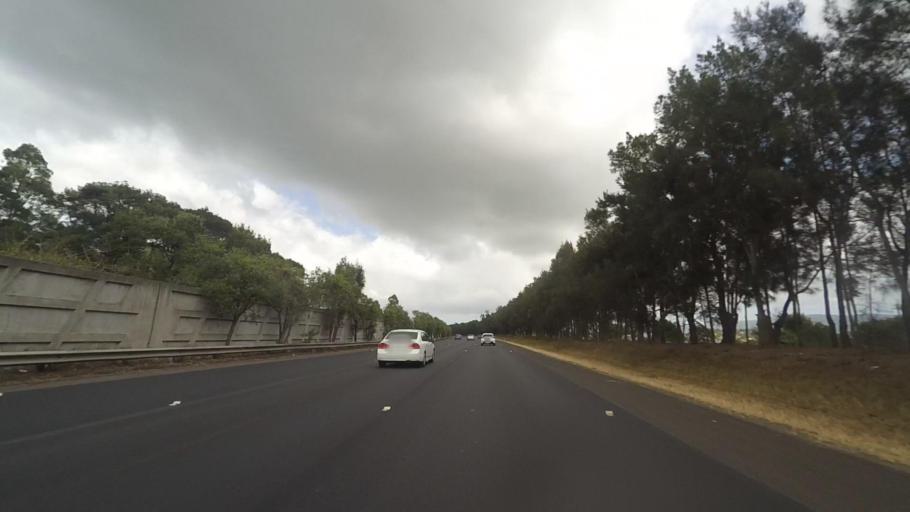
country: AU
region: New South Wales
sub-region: Wollongong
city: Berkeley
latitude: -34.4658
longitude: 150.8446
